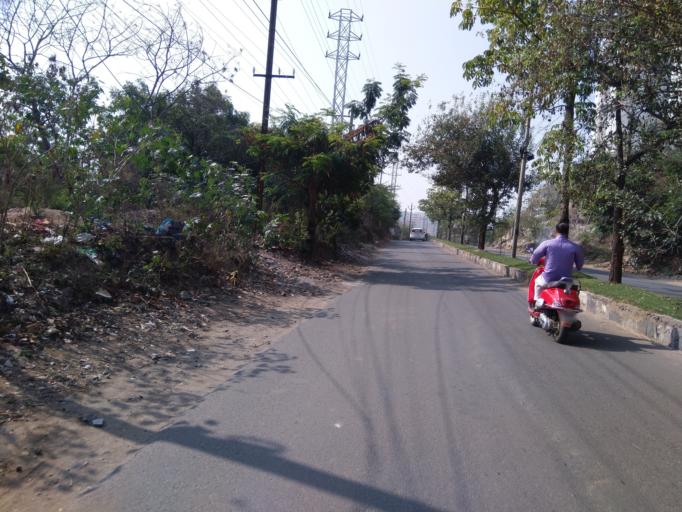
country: IN
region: Telangana
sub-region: Rangareddi
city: Kukatpalli
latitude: 17.4756
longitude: 78.3948
